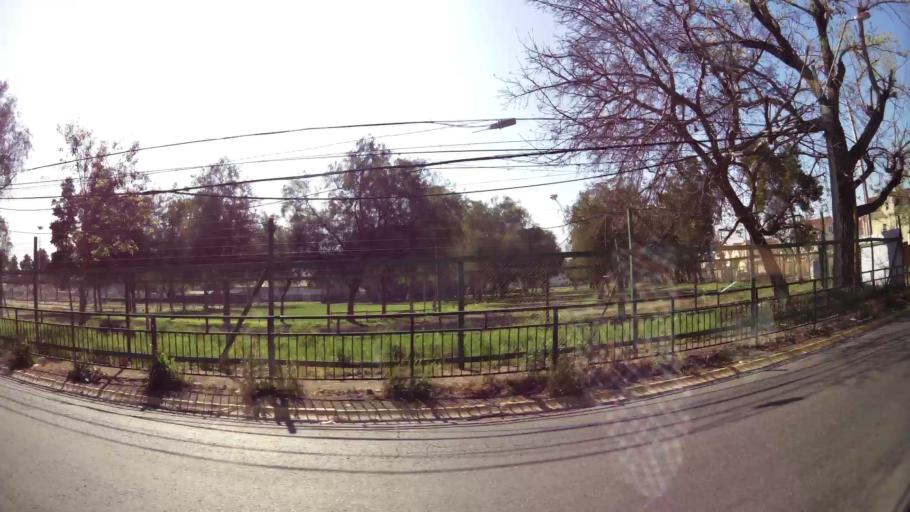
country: CL
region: Santiago Metropolitan
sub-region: Provincia de Chacabuco
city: Chicureo Abajo
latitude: -33.3605
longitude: -70.6756
